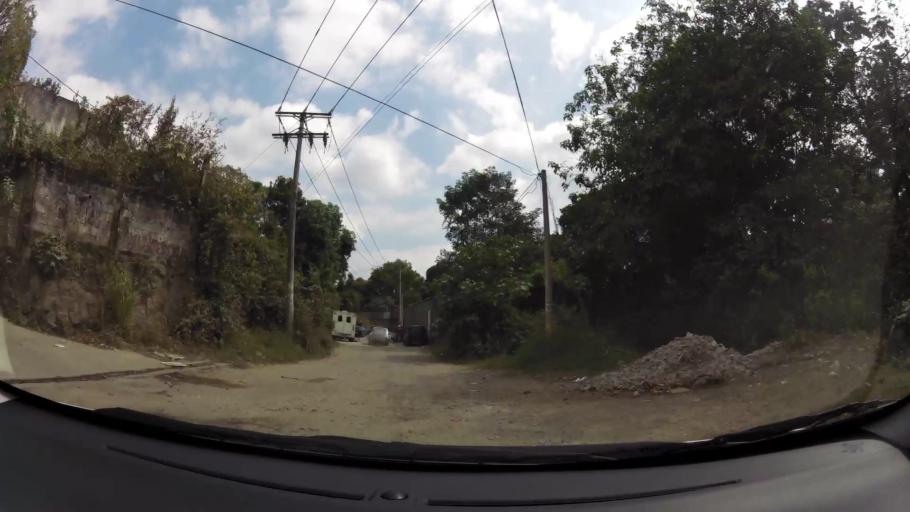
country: SV
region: San Salvador
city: Mejicanos
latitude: 13.7152
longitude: -89.2385
